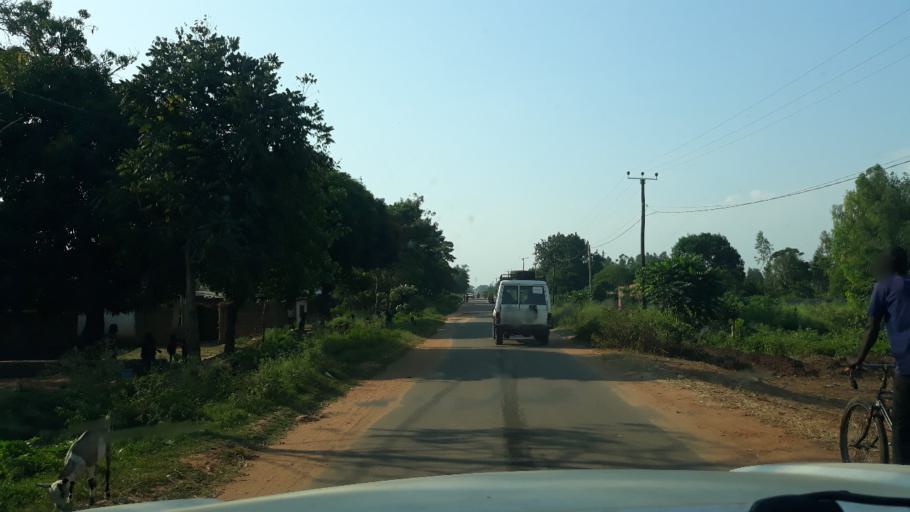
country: BI
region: Cibitoke
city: Cibitoke
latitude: -2.7541
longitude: 29.0010
